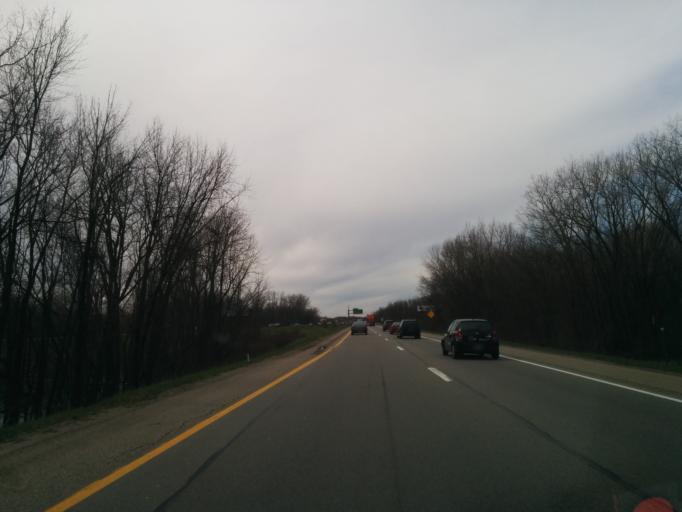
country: US
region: Michigan
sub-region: Kent County
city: Grandville
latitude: 42.9295
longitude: -85.7404
